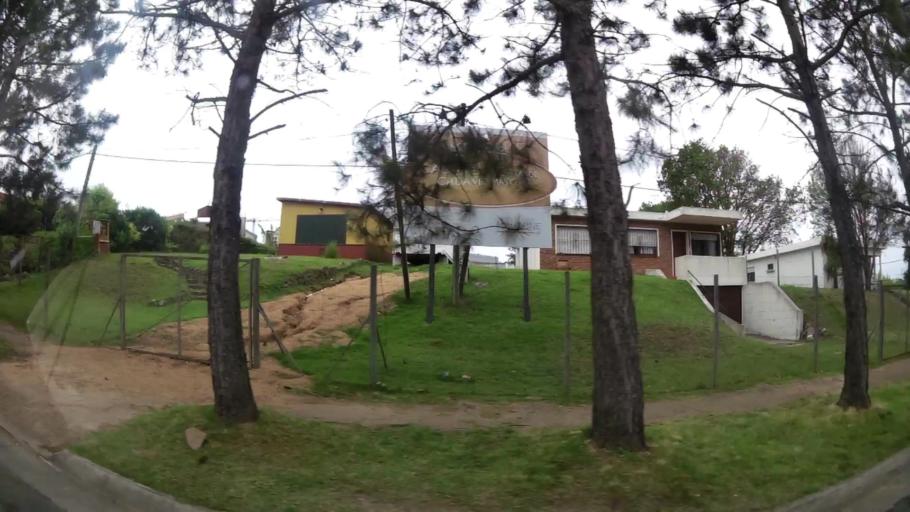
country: UY
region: Maldonado
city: Maldonado
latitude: -34.9144
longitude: -54.9627
